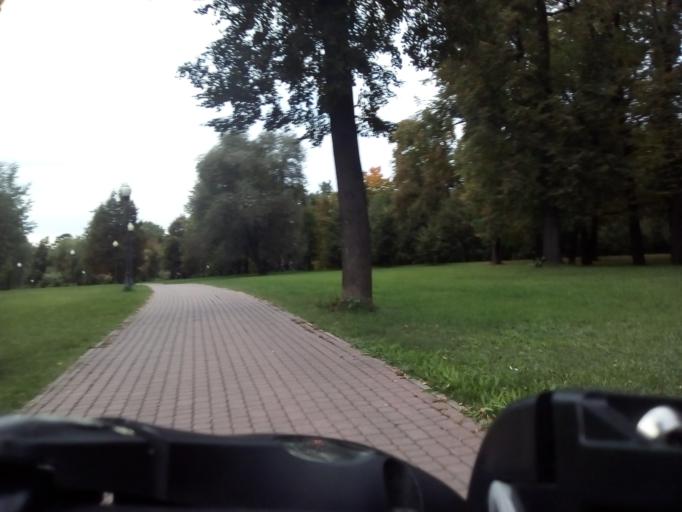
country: RU
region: Moscow
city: Sviblovo
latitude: 55.8416
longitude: 37.6410
